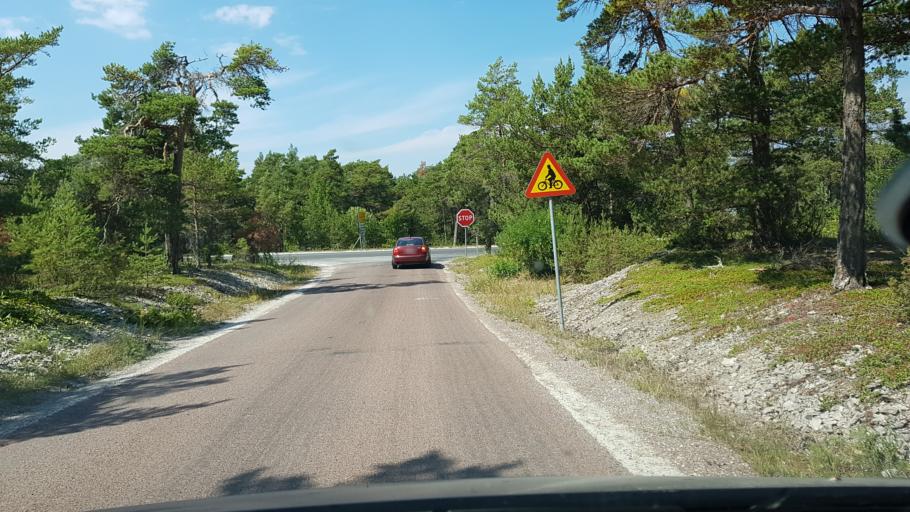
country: SE
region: Gotland
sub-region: Gotland
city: Visby
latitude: 57.6851
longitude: 18.3557
